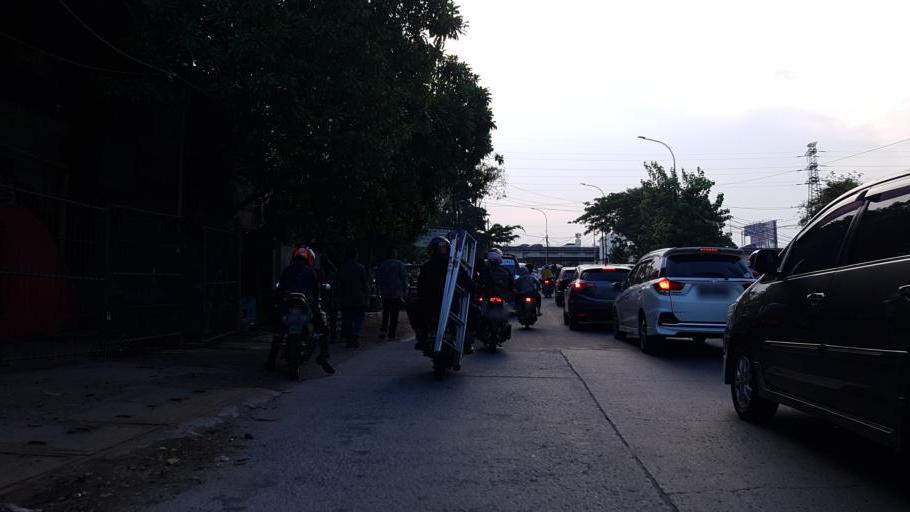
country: ID
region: Jakarta Raya
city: Jakarta
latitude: -6.1377
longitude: 106.7882
